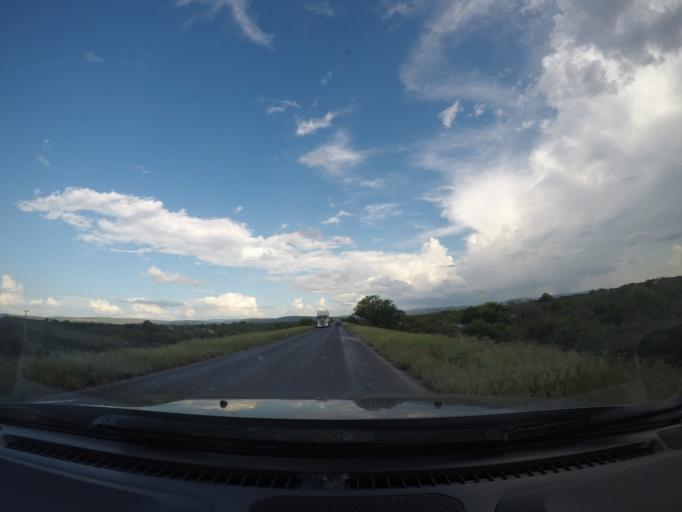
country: BR
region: Bahia
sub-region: Ibotirama
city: Ibotirama
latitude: -12.1718
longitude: -43.2616
